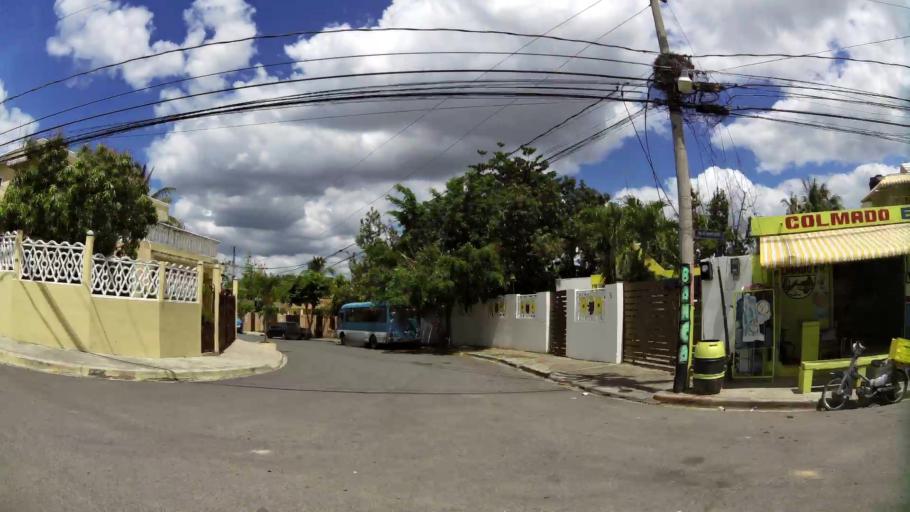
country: DO
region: Nacional
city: Ensanche Luperon
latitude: 18.5192
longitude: -69.9041
